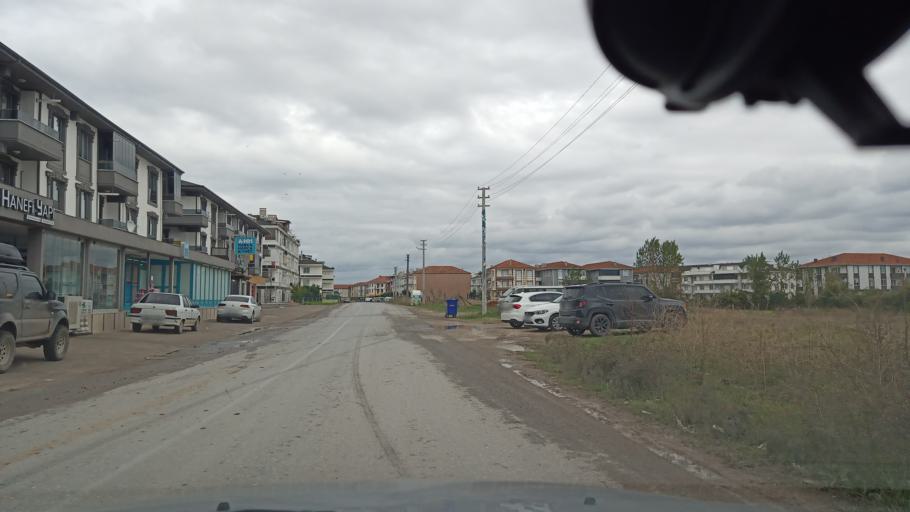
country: TR
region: Sakarya
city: Karasu
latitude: 41.1121
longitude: 30.6769
